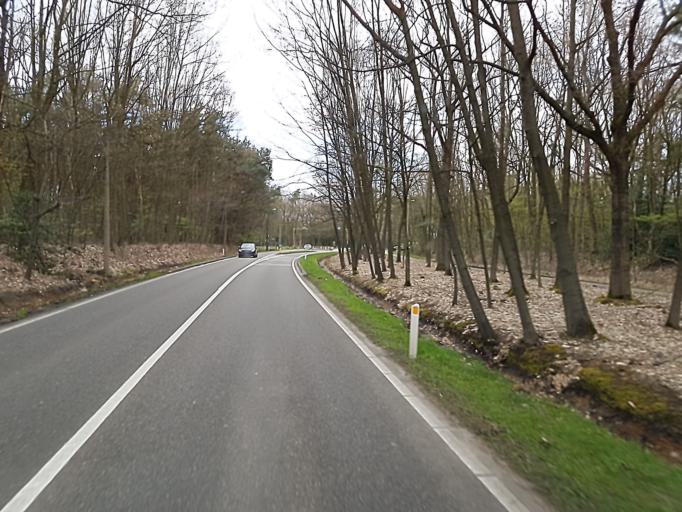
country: BE
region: Flanders
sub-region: Provincie Limburg
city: Zutendaal
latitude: 50.9581
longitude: 5.5532
